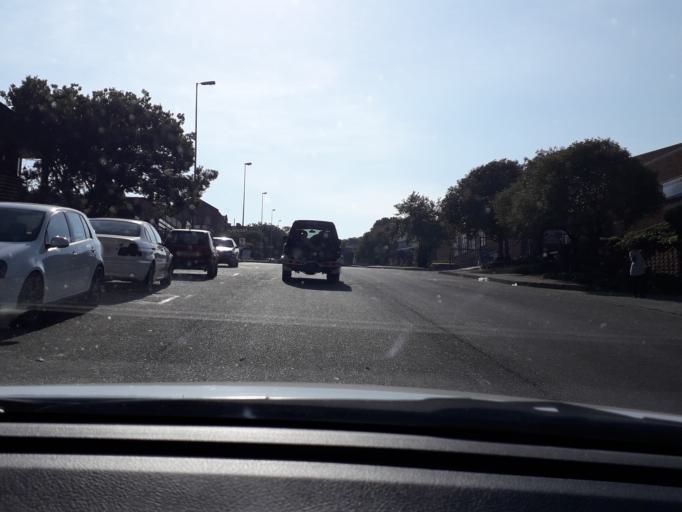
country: ZA
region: Gauteng
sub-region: City of Johannesburg Metropolitan Municipality
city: Roodepoort
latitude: -26.0831
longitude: 27.9741
